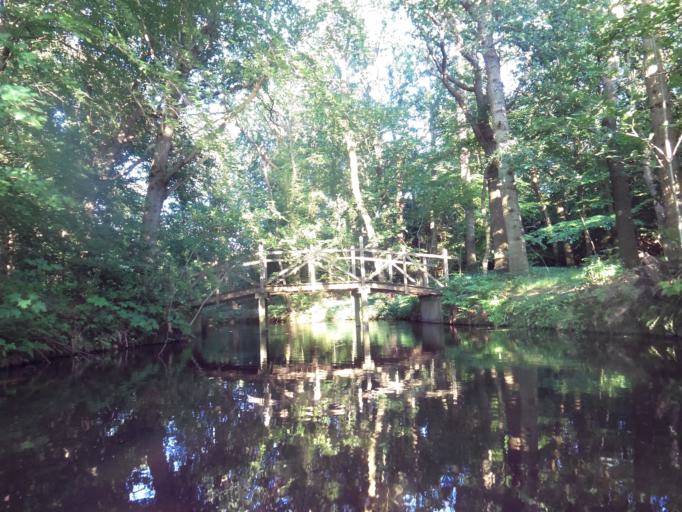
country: NL
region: South Holland
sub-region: Gemeente Wassenaar
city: Wassenaar
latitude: 52.1373
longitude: 4.3832
